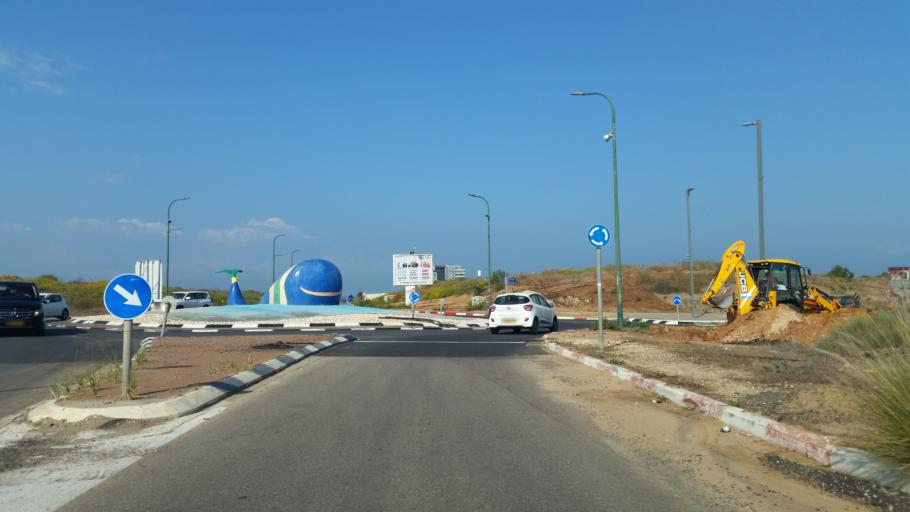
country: IL
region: Tel Aviv
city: Herzliya Pituah
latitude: 32.1552
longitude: 34.8025
